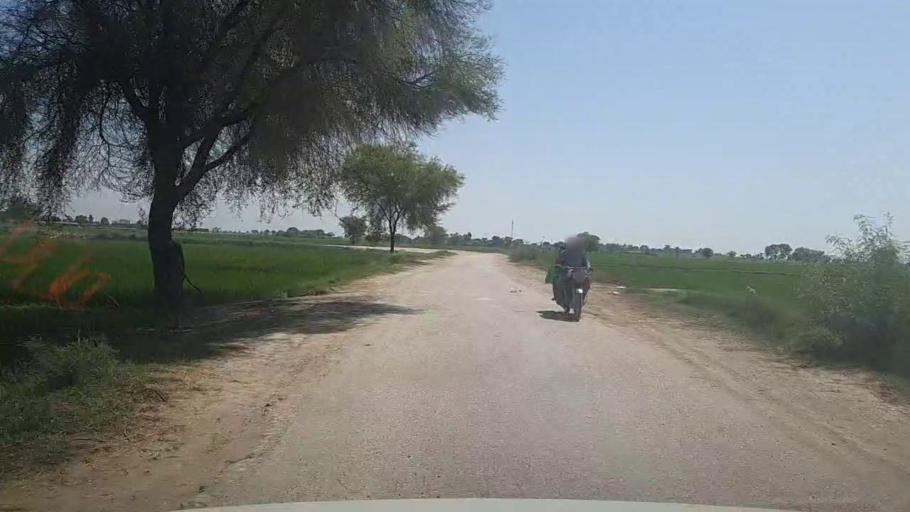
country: PK
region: Sindh
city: Kashmor
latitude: 28.2929
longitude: 69.4340
